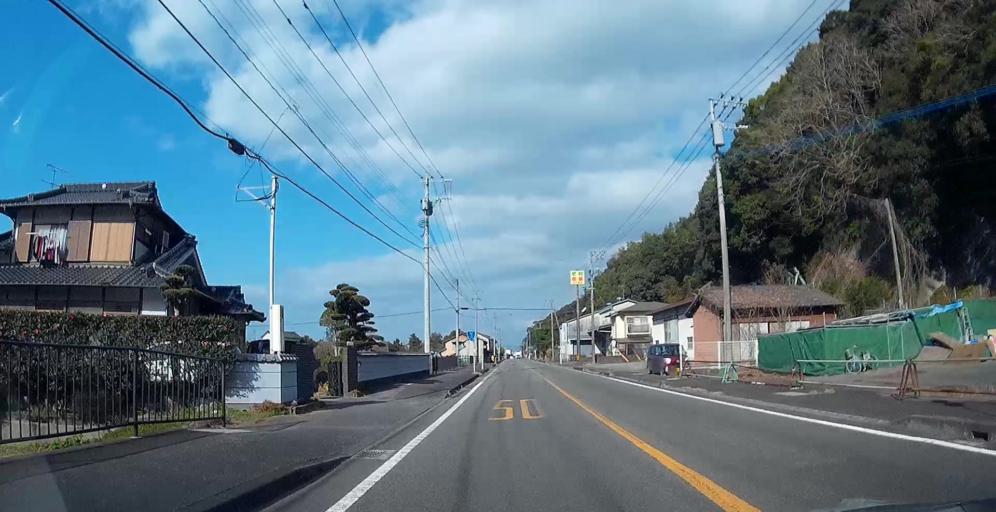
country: JP
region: Kumamoto
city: Yatsushiro
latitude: 32.4166
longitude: 130.5504
